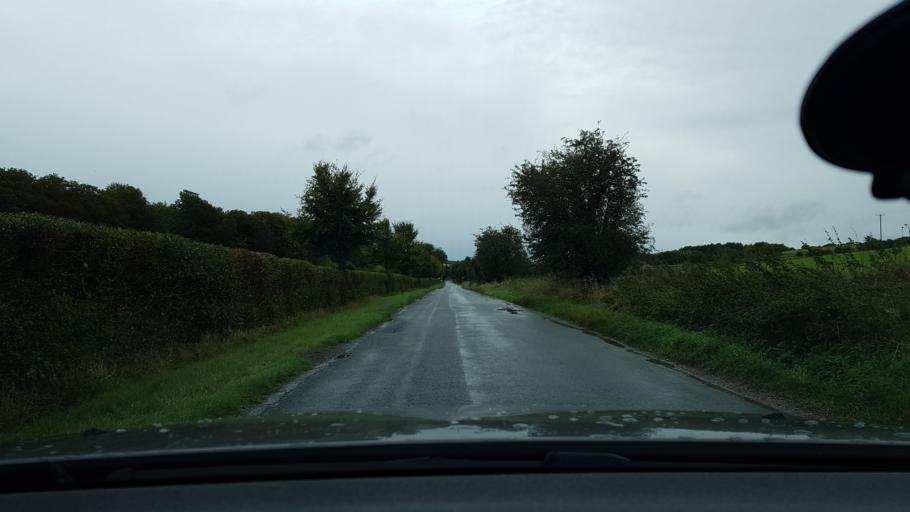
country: GB
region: England
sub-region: West Berkshire
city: Lambourn
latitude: 51.5315
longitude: -1.5262
